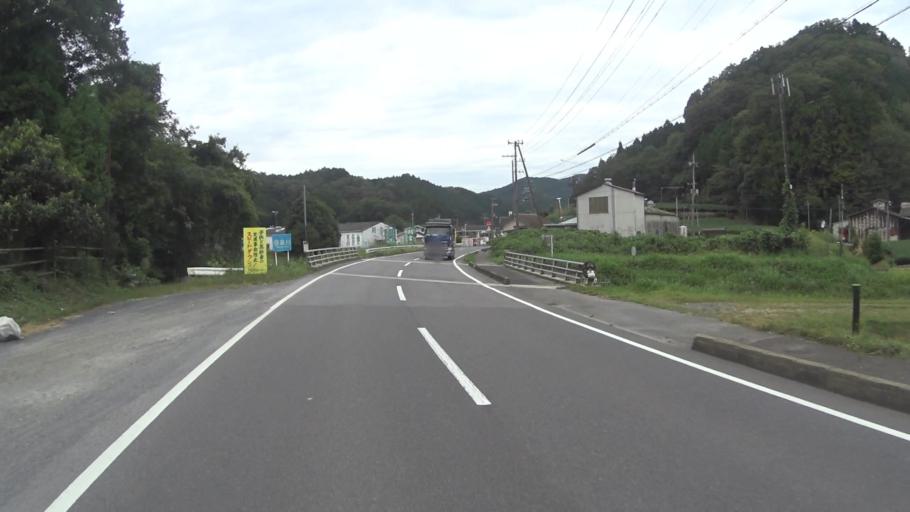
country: JP
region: Shiga Prefecture
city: Kusatsu
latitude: 34.8527
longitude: 135.9770
